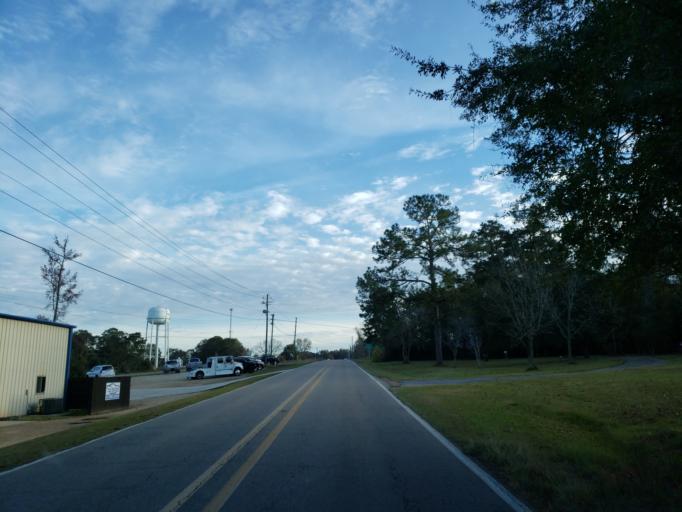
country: US
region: Mississippi
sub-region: Lamar County
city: Purvis
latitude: 31.1618
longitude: -89.4219
